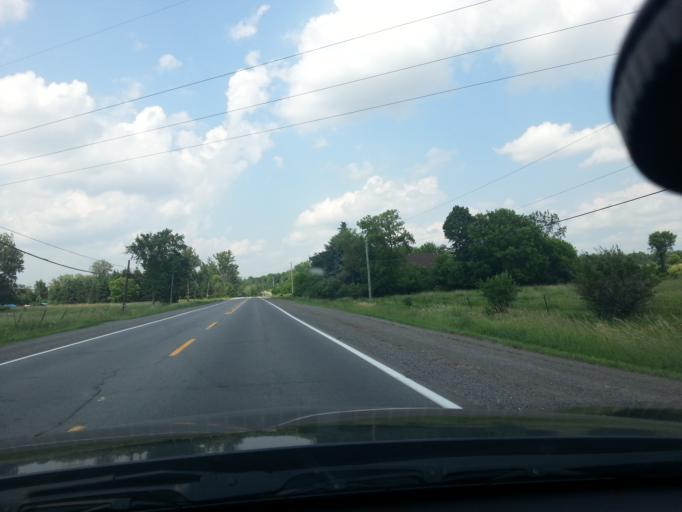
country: CA
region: Ontario
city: Ottawa
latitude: 45.3023
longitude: -75.6943
